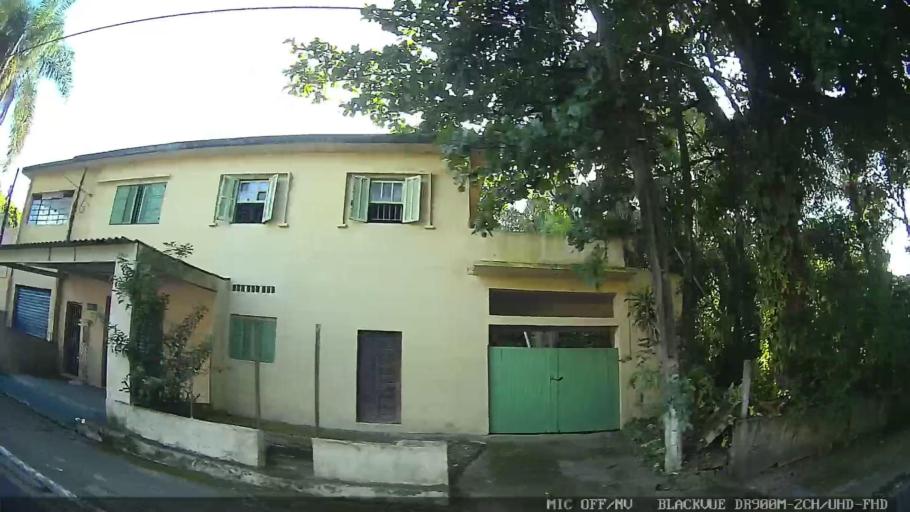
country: BR
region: Sao Paulo
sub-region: Peruibe
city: Peruibe
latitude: -24.2709
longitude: -46.9562
